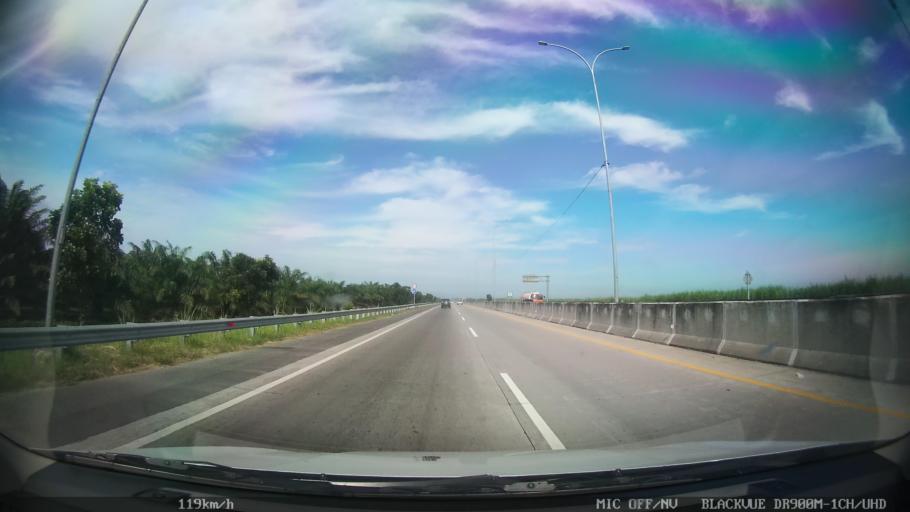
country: ID
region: North Sumatra
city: Sunggal
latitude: 3.6380
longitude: 98.6303
